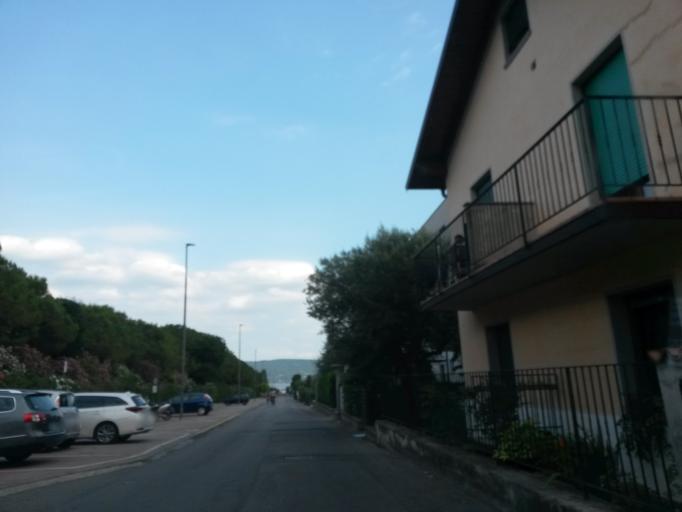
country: IT
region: Lombardy
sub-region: Provincia di Brescia
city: Toscolano Maderno
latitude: 45.6408
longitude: 10.6156
